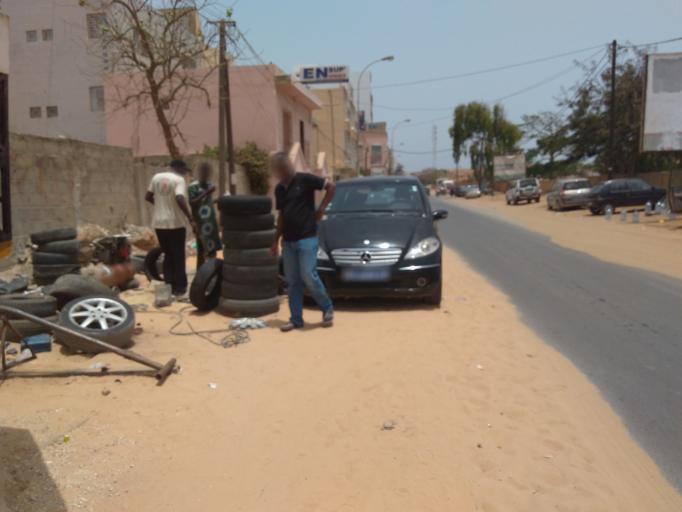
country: SN
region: Dakar
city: Grand Dakar
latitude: 14.7302
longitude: -17.4656
